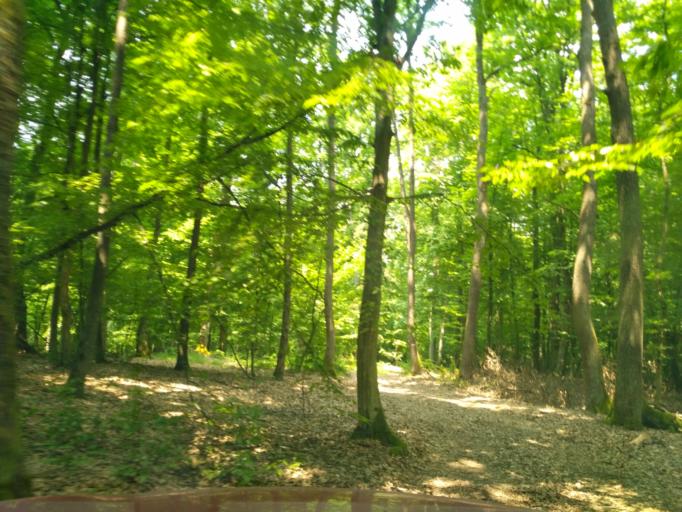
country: SK
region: Kosicky
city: Moldava nad Bodvou
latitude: 48.6545
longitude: 21.0343
